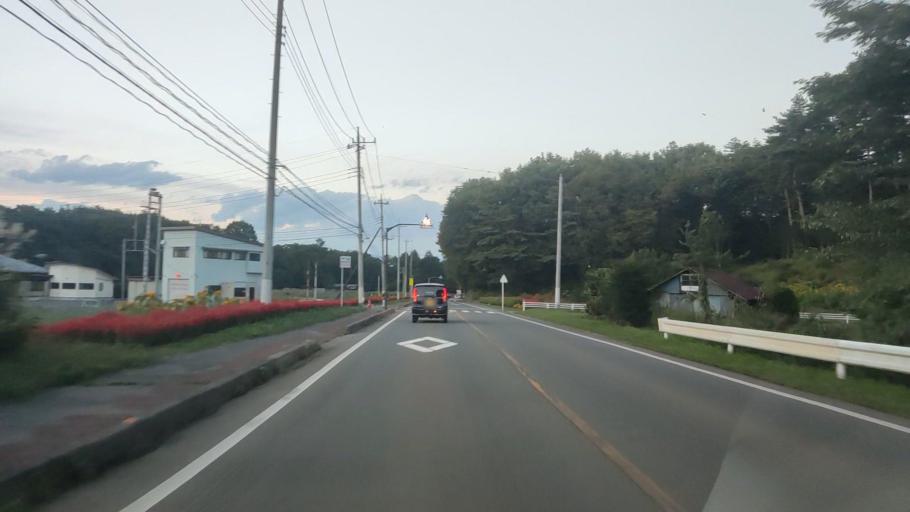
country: JP
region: Nagano
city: Komoro
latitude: 36.5090
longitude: 138.5940
